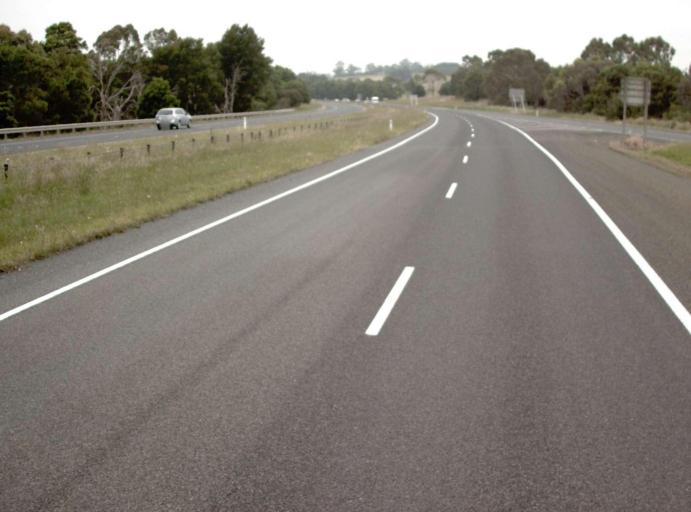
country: AU
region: Victoria
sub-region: Baw Baw
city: Warragul
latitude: -38.1448
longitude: 145.8847
